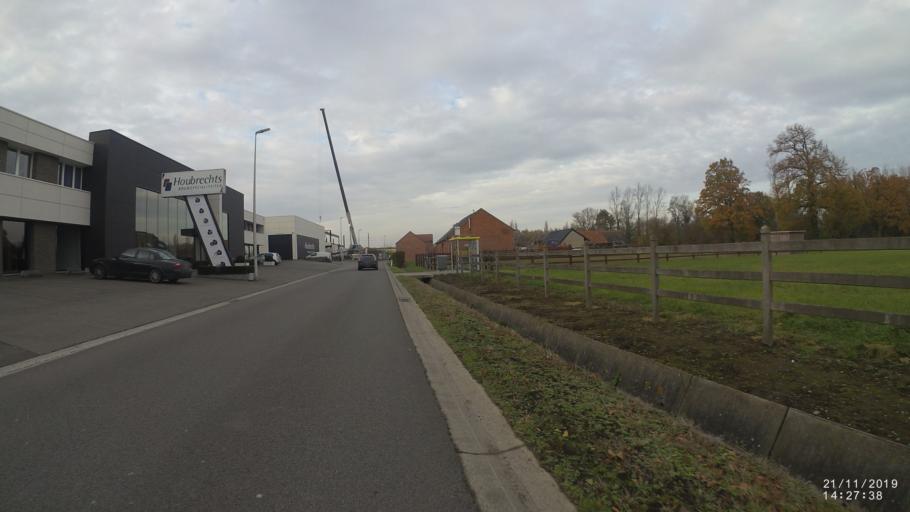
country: BE
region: Flanders
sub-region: Provincie Limburg
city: Alken
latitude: 50.8914
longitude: 5.3059
